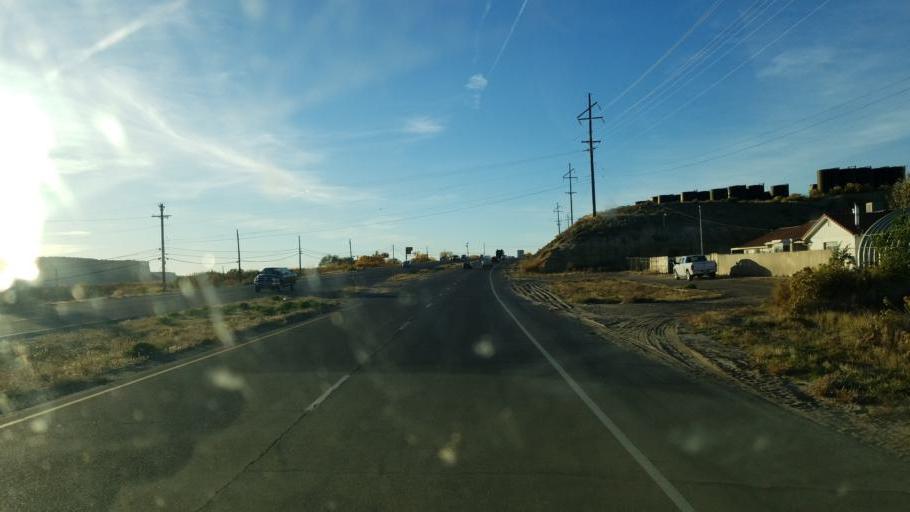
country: US
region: New Mexico
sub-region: San Juan County
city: Farmington
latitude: 36.7112
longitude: -108.1398
